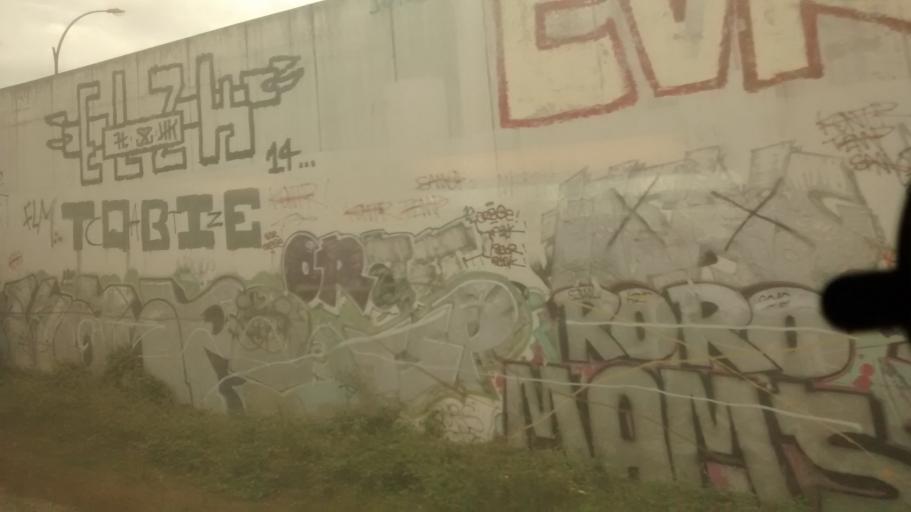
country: FR
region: Ile-de-France
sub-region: Departement de l'Essonne
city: Massy
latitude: 48.7352
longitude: 2.2756
